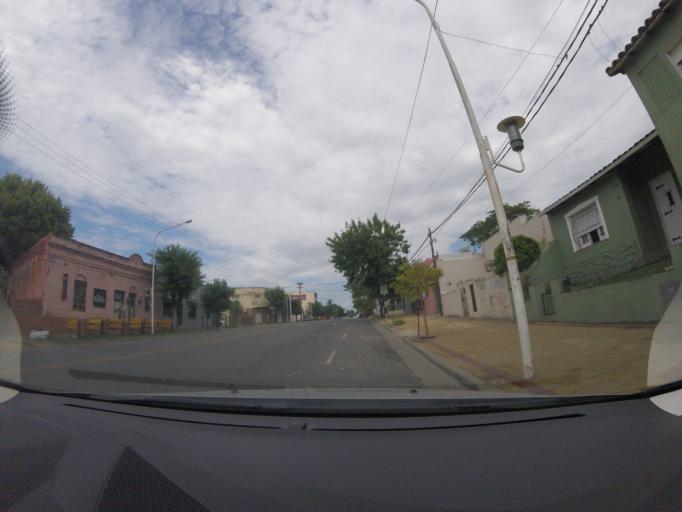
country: AR
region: Buenos Aires
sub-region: Partido de Tandil
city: Tandil
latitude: -37.3339
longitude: -59.1332
